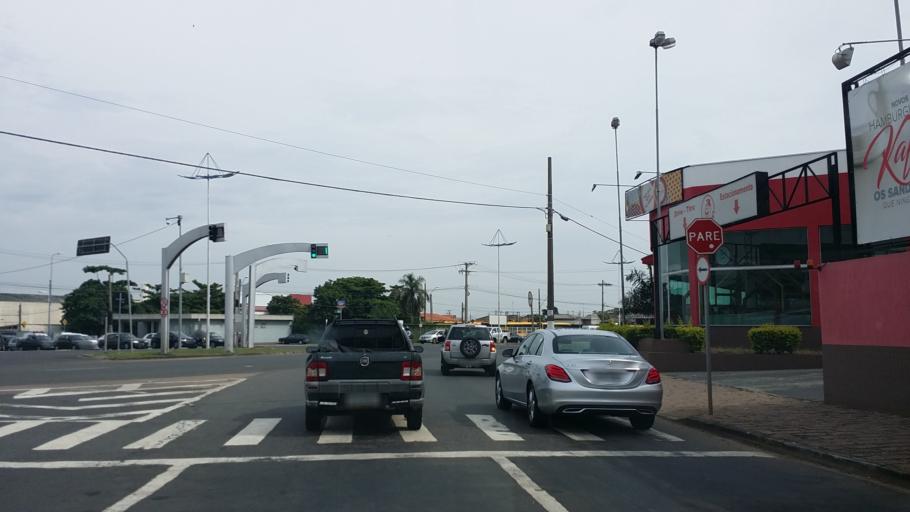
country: BR
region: Sao Paulo
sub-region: Indaiatuba
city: Indaiatuba
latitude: -23.1200
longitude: -47.2240
